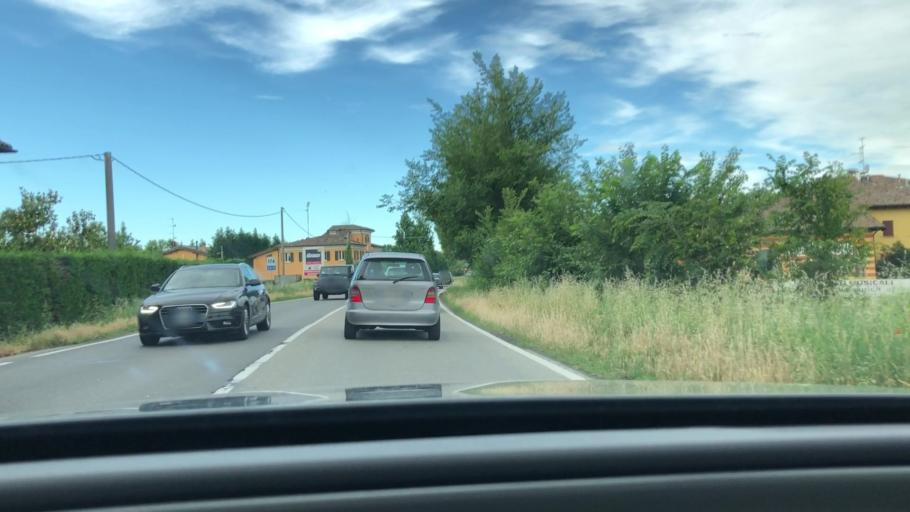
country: IT
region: Emilia-Romagna
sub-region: Provincia di Modena
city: San Damaso
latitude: 44.6090
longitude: 10.9356
